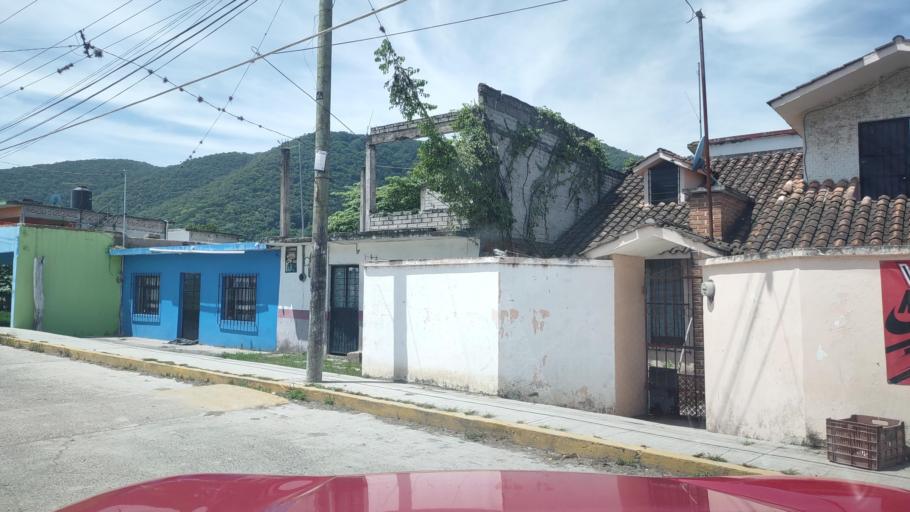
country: MX
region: Veracruz
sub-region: Emiliano Zapata
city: Dos Rios
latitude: 19.4272
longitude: -96.7977
